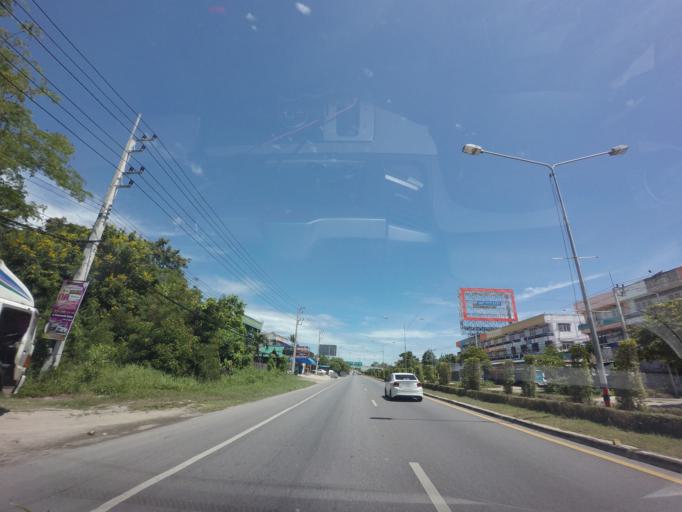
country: TH
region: Phetchaburi
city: Cha-am
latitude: 12.8061
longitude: 99.9496
